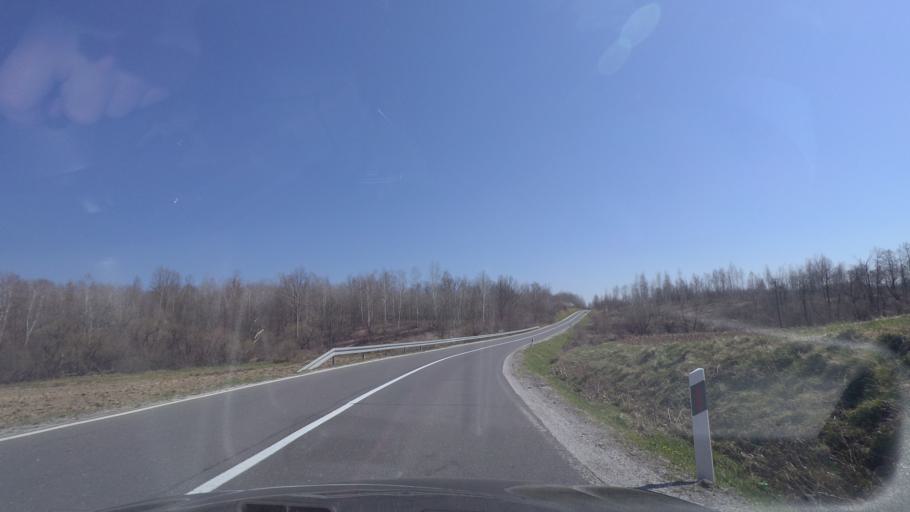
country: HR
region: Sisacko-Moslavacka
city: Gvozd
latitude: 45.3286
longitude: 15.9357
